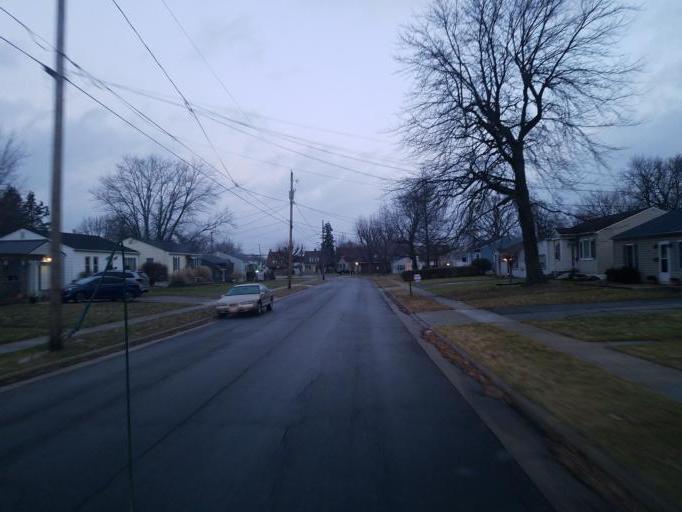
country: US
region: Ohio
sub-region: Marion County
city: Marion
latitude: 40.5770
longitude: -83.1360
